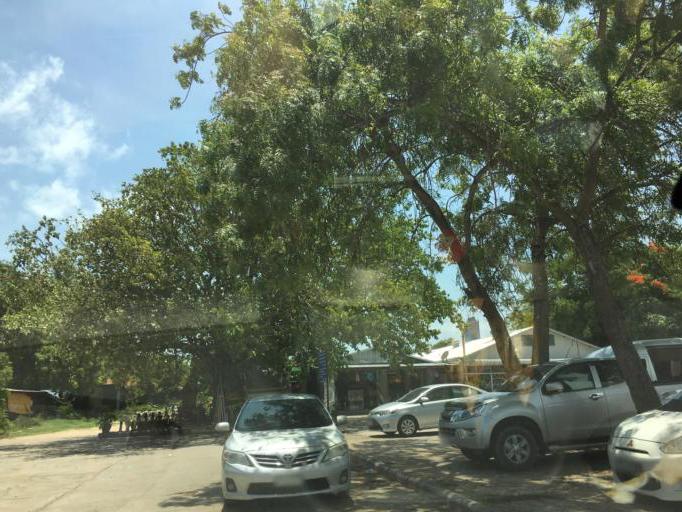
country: TH
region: Chon Buri
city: Phatthaya
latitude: 12.8985
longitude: 100.8755
